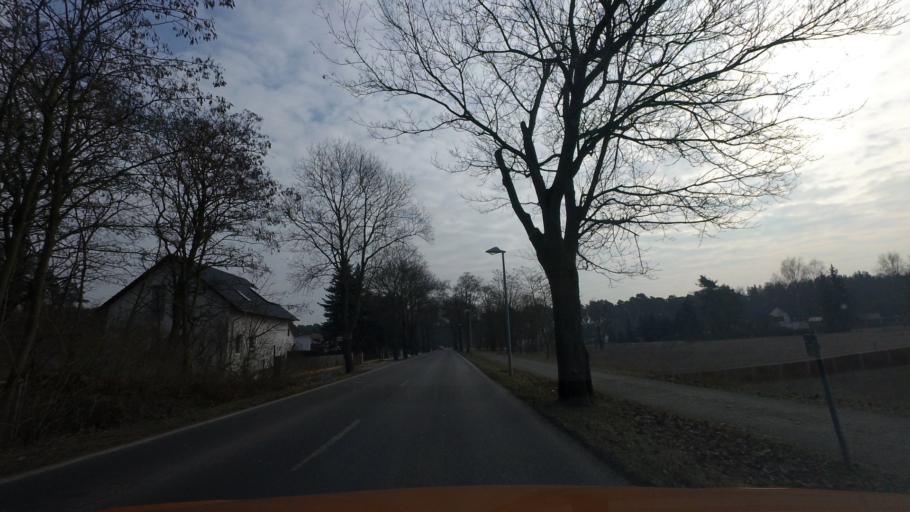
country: DE
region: Brandenburg
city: Zossen
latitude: 52.2455
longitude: 13.4213
